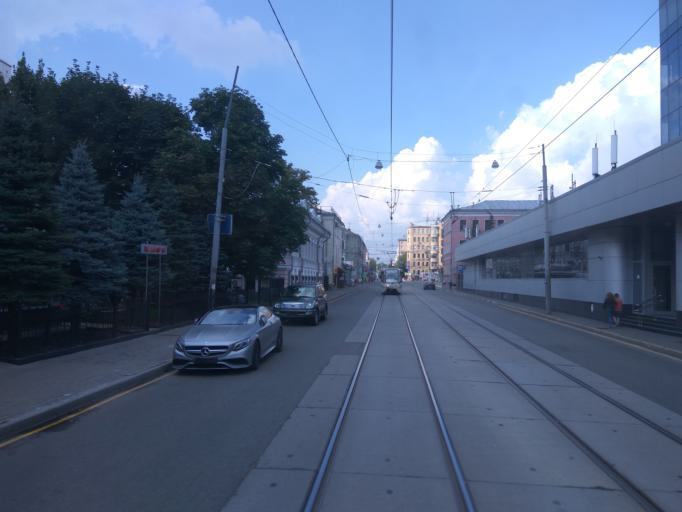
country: RU
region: Moscow
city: Lefortovo
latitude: 55.7676
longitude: 37.6797
